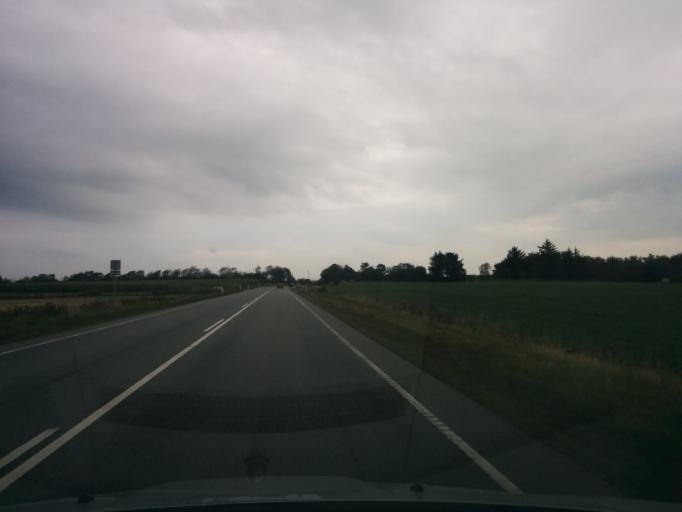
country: DK
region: South Denmark
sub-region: Esbjerg Kommune
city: Bramming
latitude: 55.5610
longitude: 8.6493
